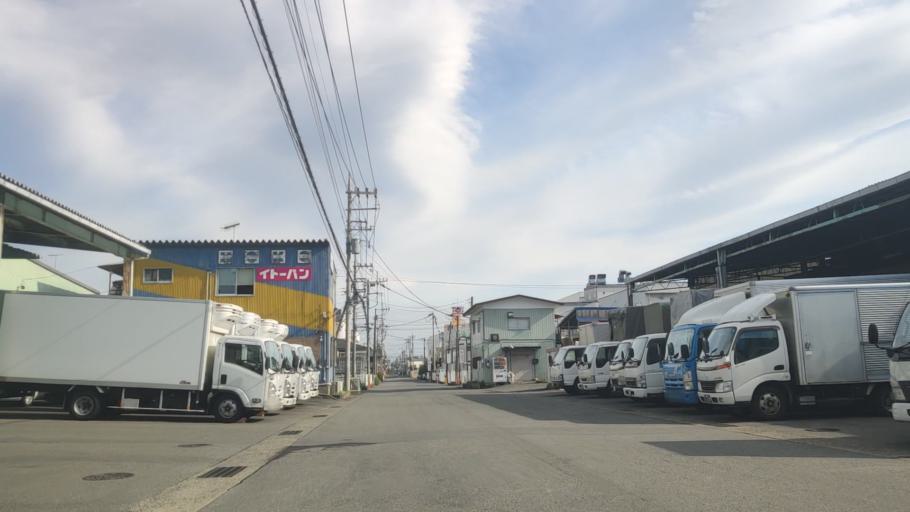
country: JP
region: Kanagawa
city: Atsugi
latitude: 35.4269
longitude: 139.3595
